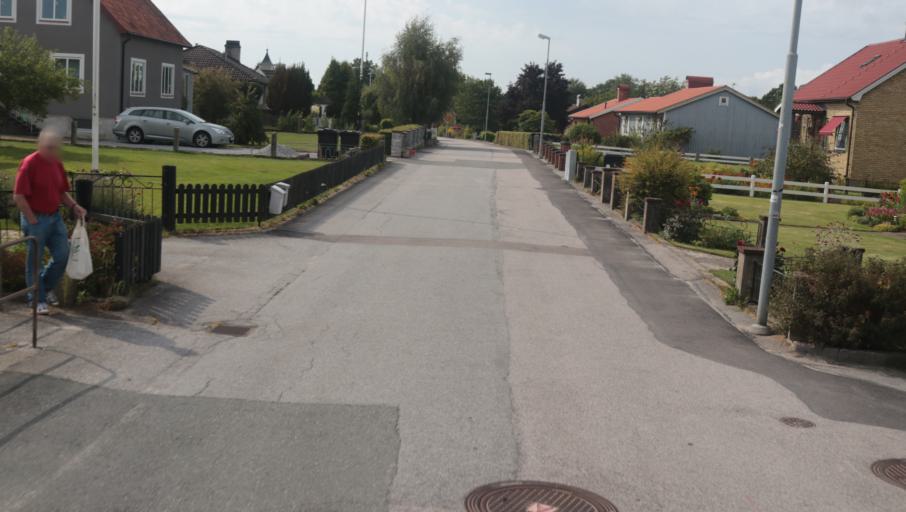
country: SE
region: Blekinge
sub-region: Karlshamns Kommun
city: Morrum
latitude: 56.1981
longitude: 14.7512
